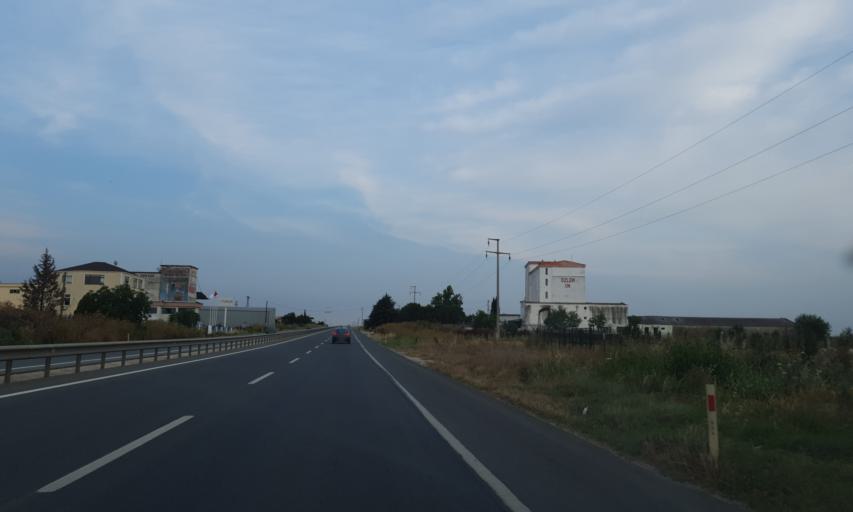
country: TR
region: Kirklareli
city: Luleburgaz
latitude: 41.3680
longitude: 27.4114
